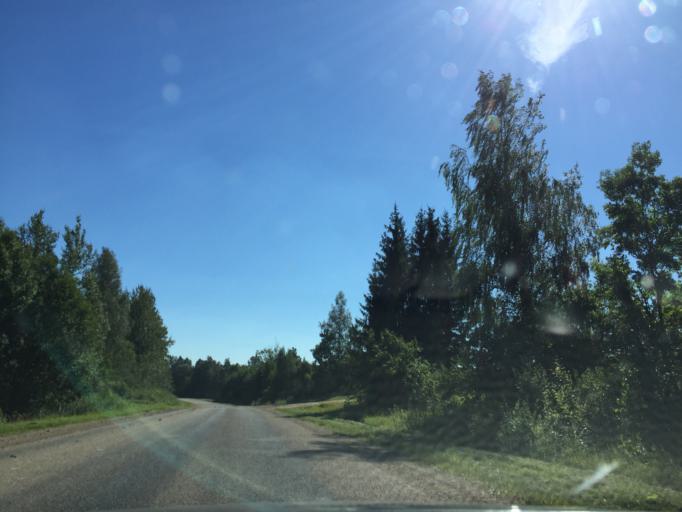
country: LV
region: Akniste
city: Akniste
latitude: 56.0400
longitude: 25.9082
